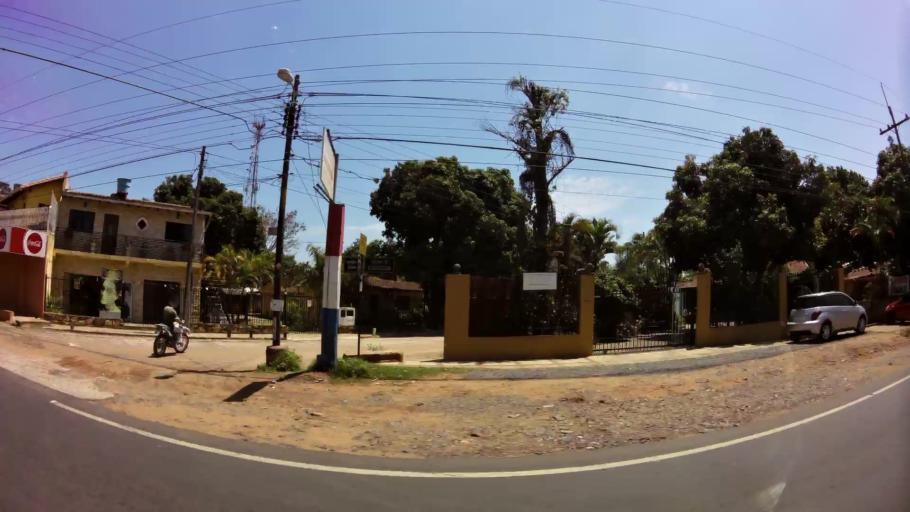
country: PY
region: Central
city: San Antonio
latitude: -25.4081
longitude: -57.5455
